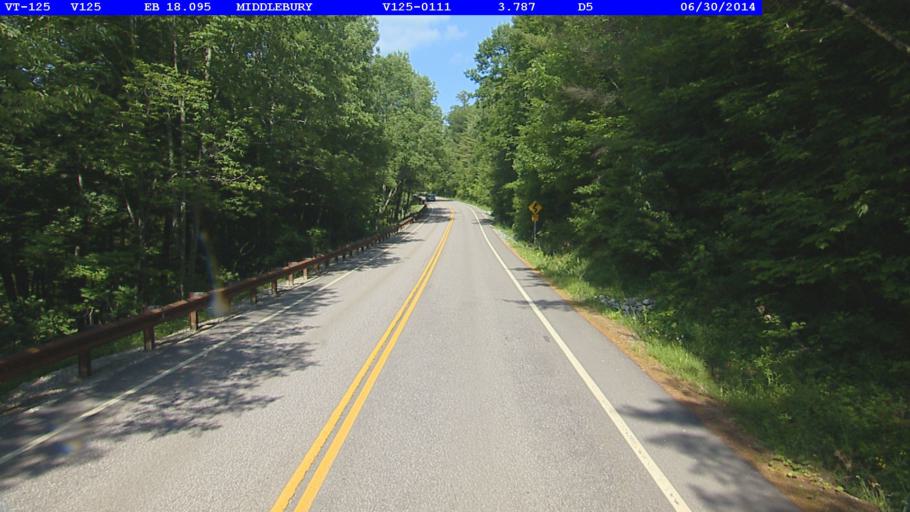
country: US
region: Vermont
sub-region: Addison County
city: Middlebury (village)
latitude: 43.9734
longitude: -73.0684
